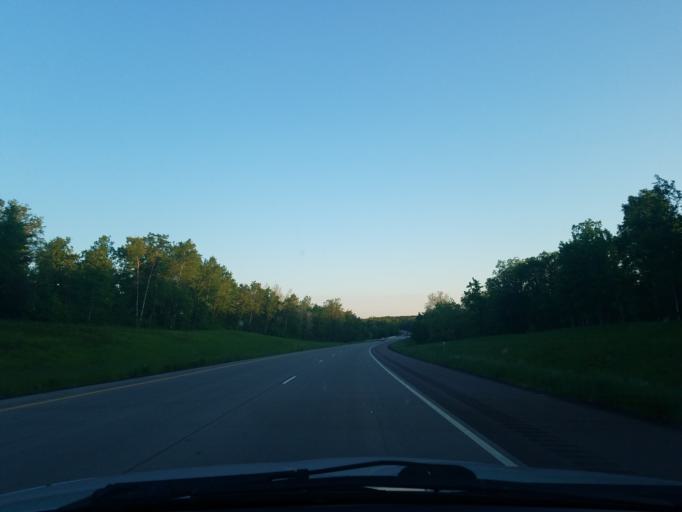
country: US
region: Minnesota
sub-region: Pine County
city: Sandstone
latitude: 46.2243
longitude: -92.8301
